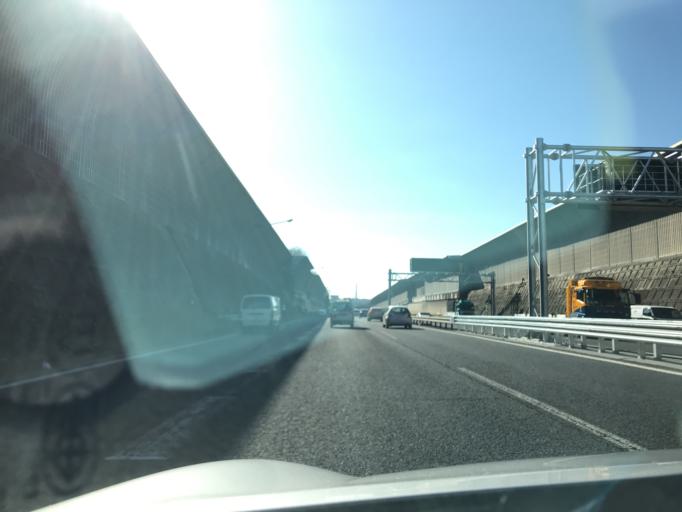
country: JP
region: Chiba
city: Chiba
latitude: 35.6532
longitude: 140.1070
